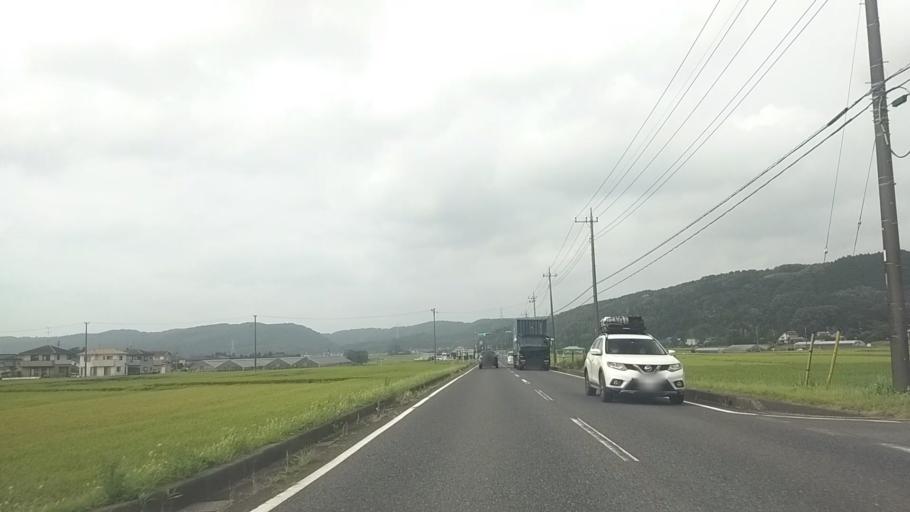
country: JP
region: Chiba
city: Kimitsu
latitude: 35.2881
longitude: 139.9903
